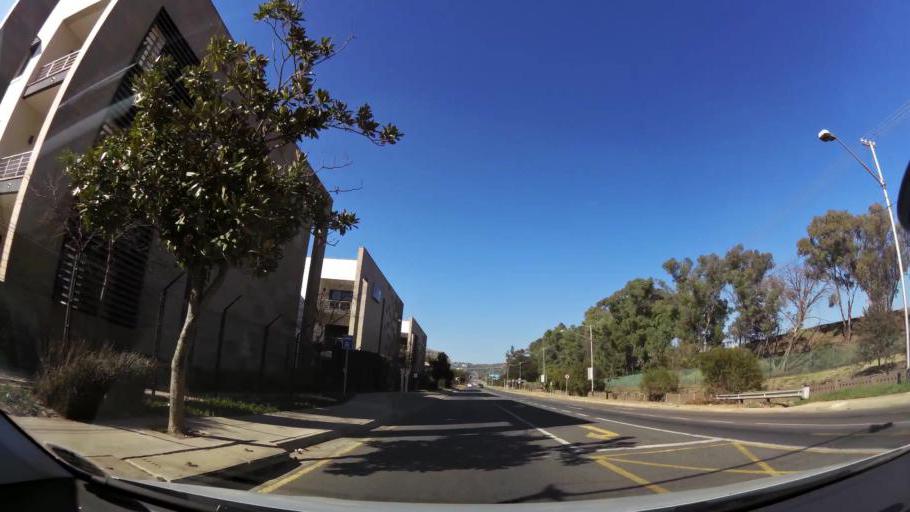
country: ZA
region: Gauteng
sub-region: City of Tshwane Metropolitan Municipality
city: Pretoria
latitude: -25.7669
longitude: 28.2218
